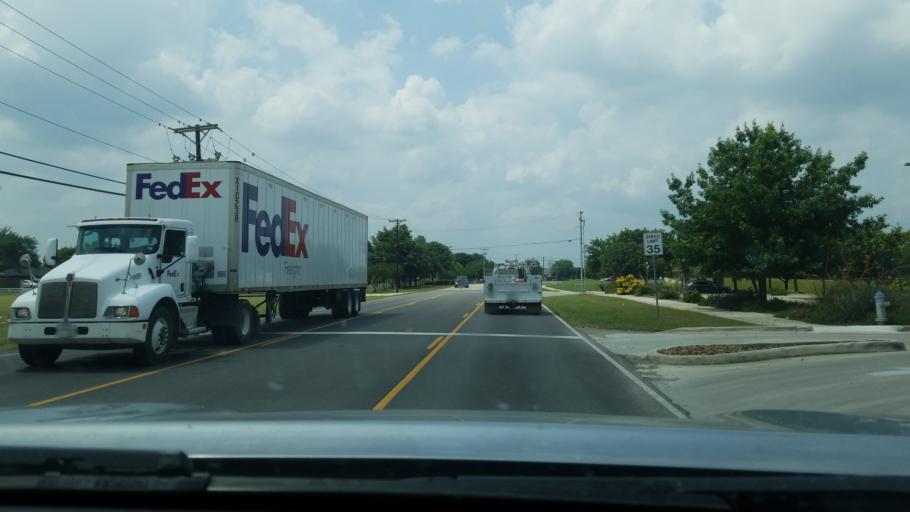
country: US
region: Texas
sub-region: Comal County
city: New Braunfels
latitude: 29.7314
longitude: -98.0972
